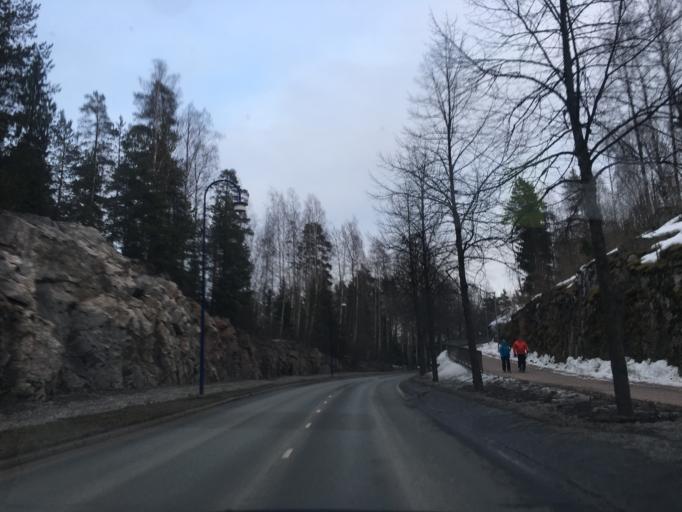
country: FI
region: Uusimaa
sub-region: Helsinki
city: Vantaa
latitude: 60.3246
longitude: 25.0716
